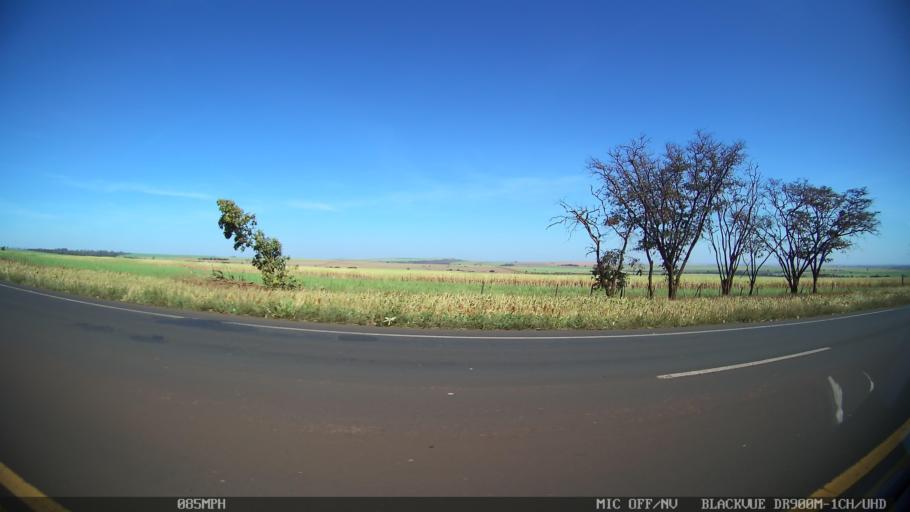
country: BR
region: Sao Paulo
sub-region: Ipua
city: Ipua
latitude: -20.4722
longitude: -48.1054
